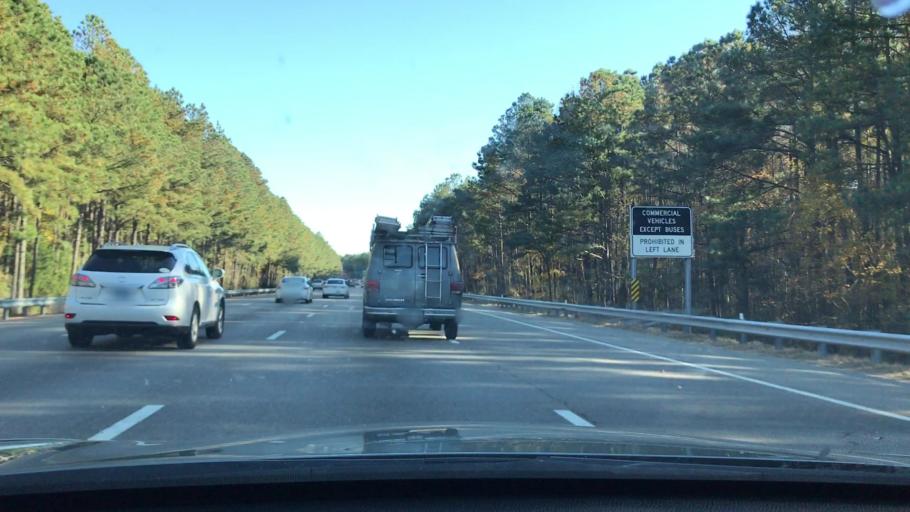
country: US
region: Virginia
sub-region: Henrico County
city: Glen Allen
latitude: 37.6641
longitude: -77.4799
